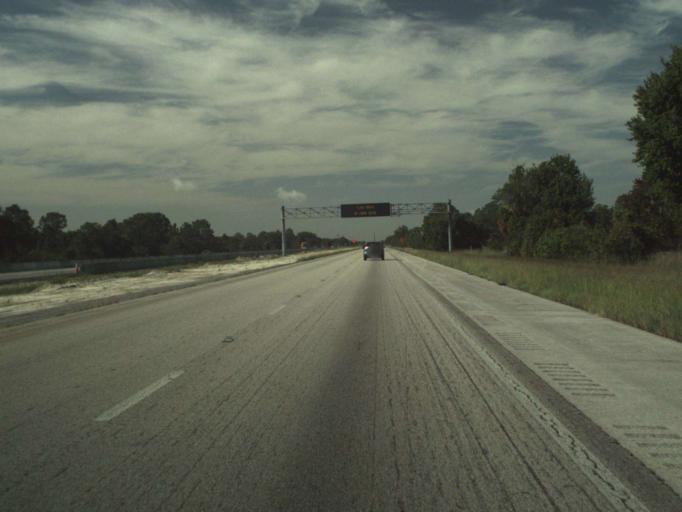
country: US
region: Florida
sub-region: Indian River County
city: Fellsmere
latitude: 27.7939
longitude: -80.5498
